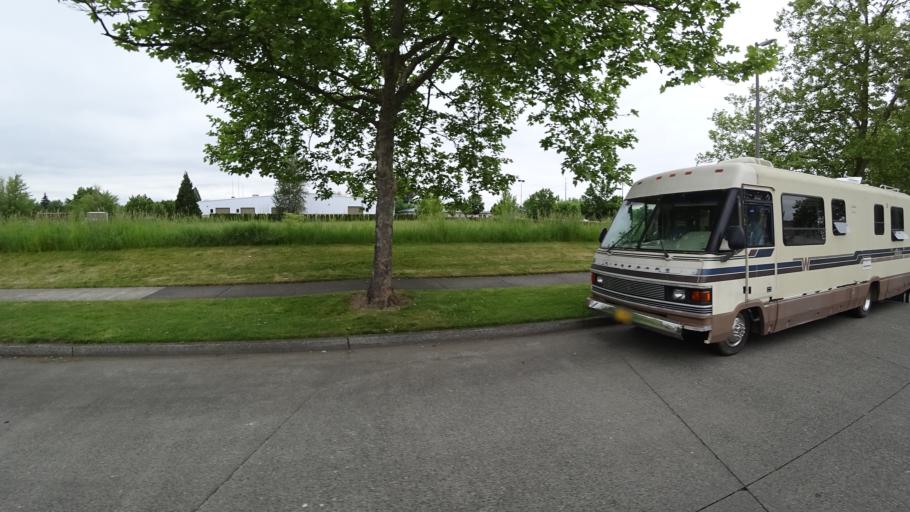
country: US
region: Oregon
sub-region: Washington County
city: Aloha
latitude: 45.4977
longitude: -122.9226
